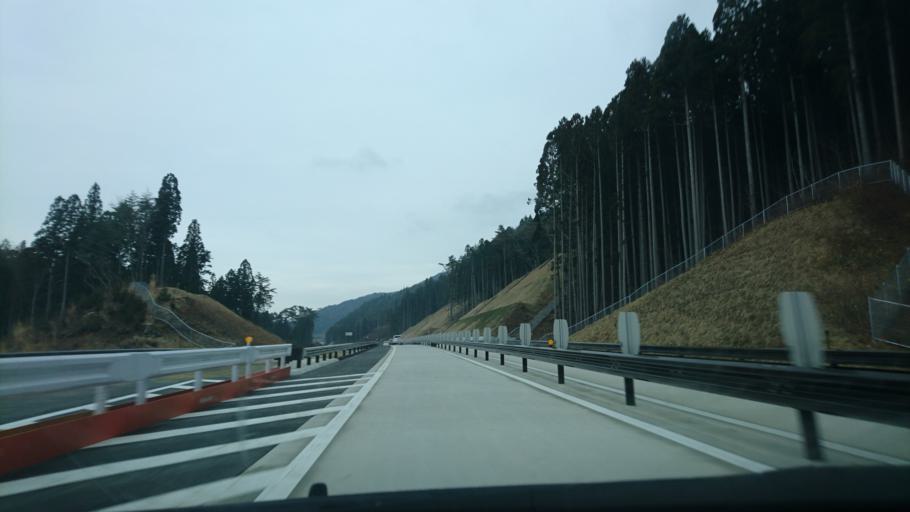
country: JP
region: Iwate
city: Ofunato
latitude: 38.9619
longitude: 141.6245
